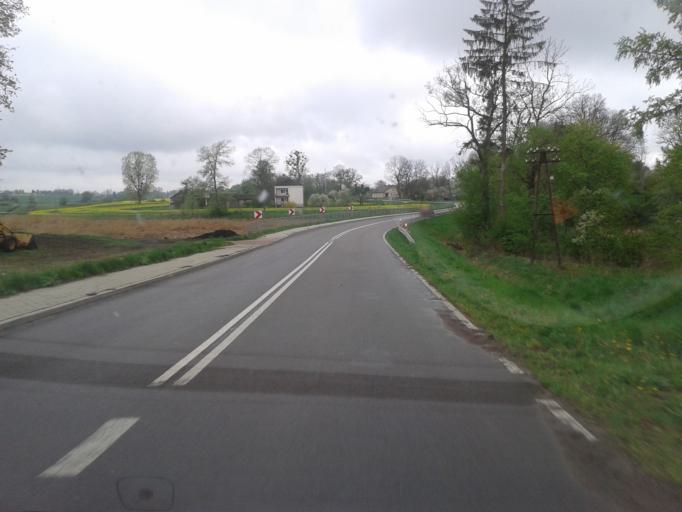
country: PL
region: Lublin Voivodeship
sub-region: Powiat hrubieszowski
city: Dolhobyczow
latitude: 50.5874
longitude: 24.0004
